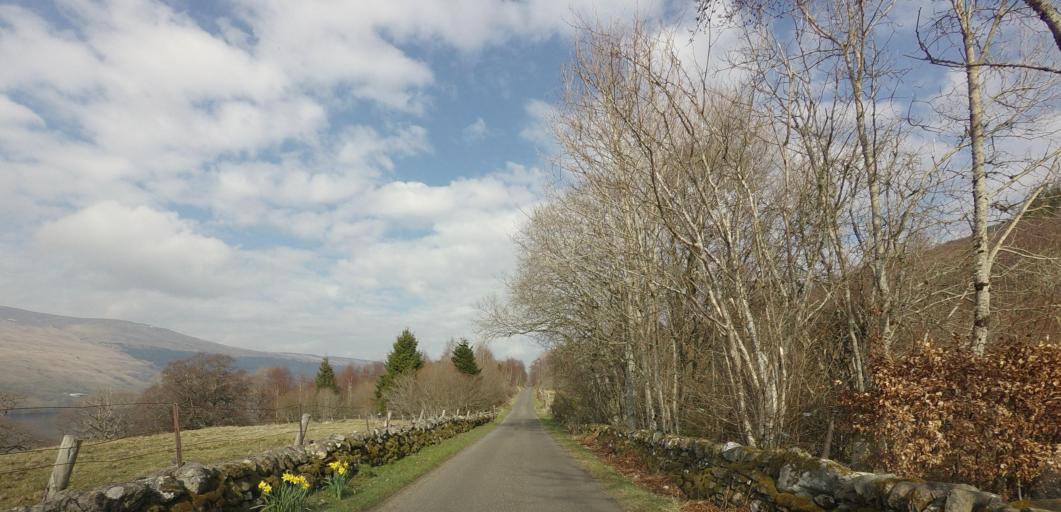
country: GB
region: Scotland
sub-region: Perth and Kinross
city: Comrie
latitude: 56.5317
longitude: -4.1084
